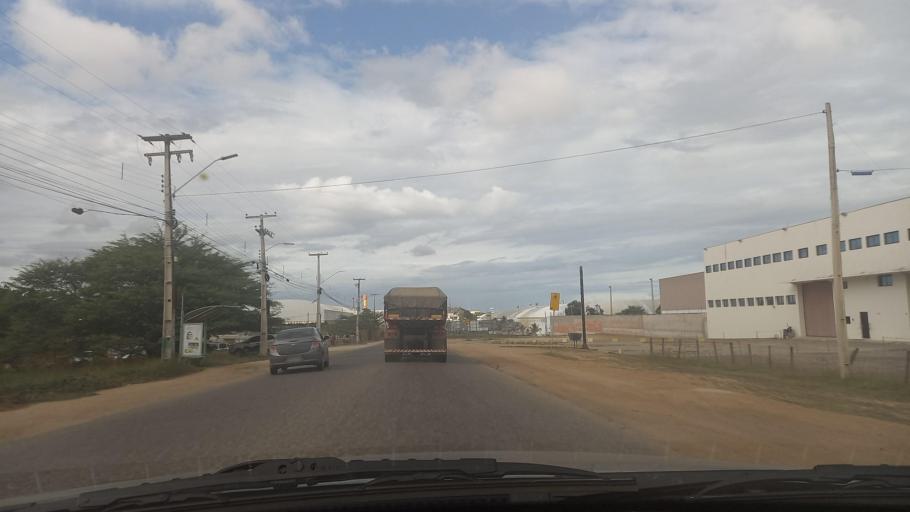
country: BR
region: Pernambuco
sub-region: Caruaru
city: Caruaru
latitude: -8.2900
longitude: -36.0182
